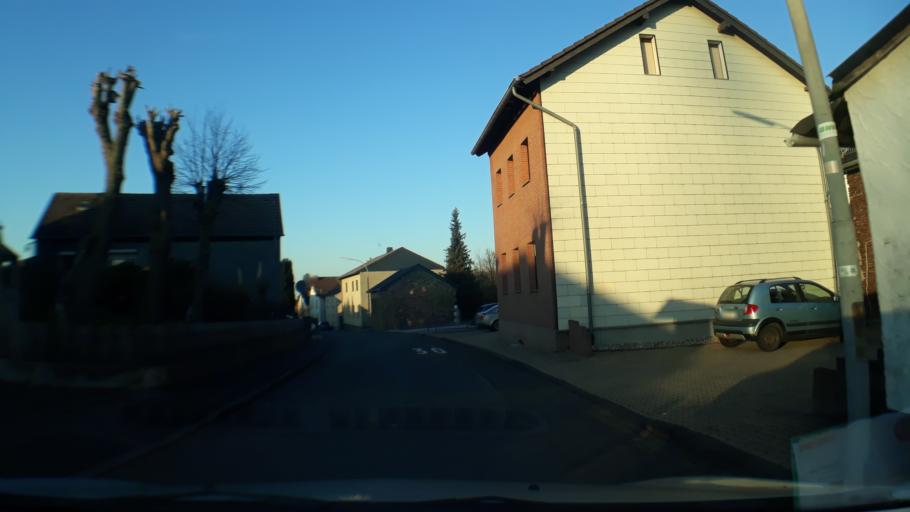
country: DE
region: North Rhine-Westphalia
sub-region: Regierungsbezirk Koln
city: Kall
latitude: 50.5678
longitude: 6.5986
